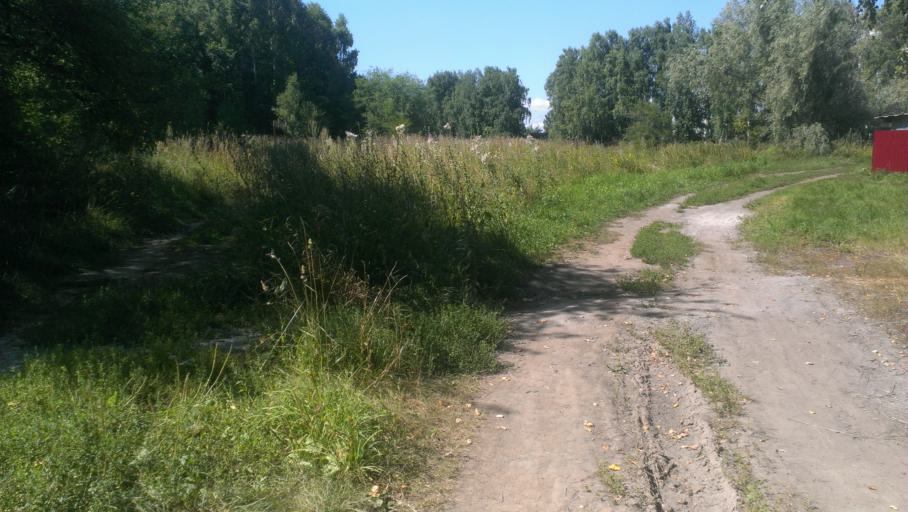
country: RU
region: Altai Krai
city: Nauchnyy Gorodok
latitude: 53.4235
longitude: 83.5107
